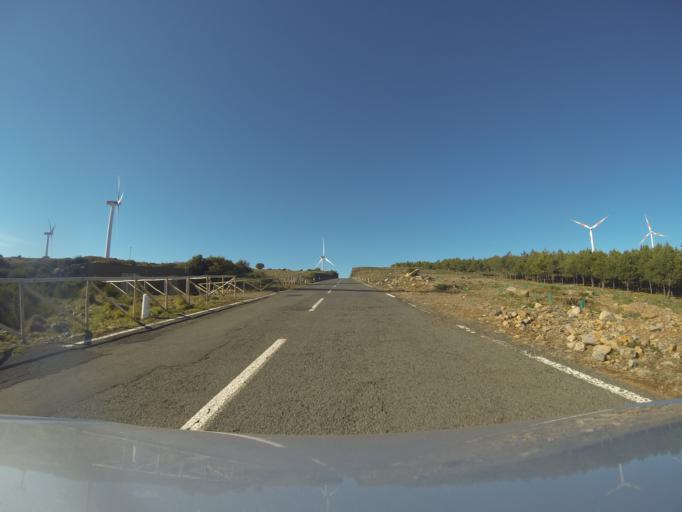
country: PT
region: Madeira
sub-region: Sao Vicente
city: Sao Vicente
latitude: 32.7463
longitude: -17.0576
